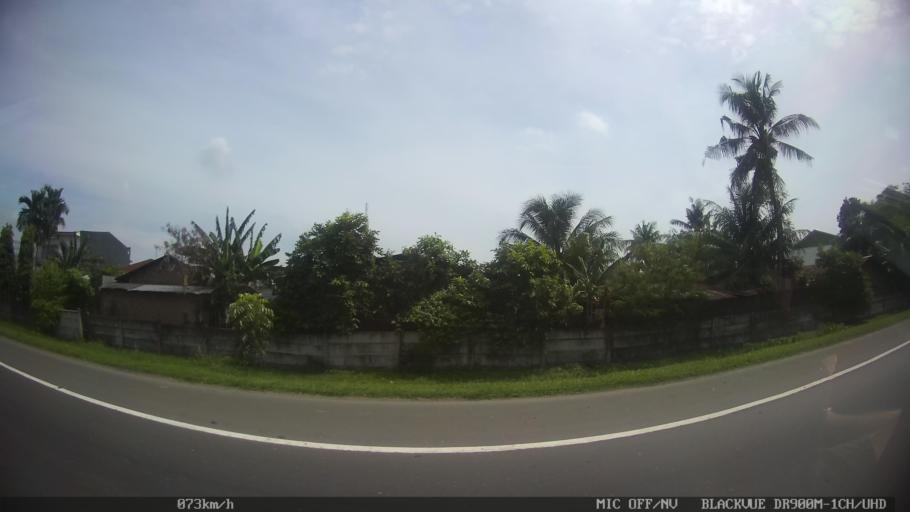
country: ID
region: North Sumatra
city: Medan
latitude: 3.6439
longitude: 98.6913
